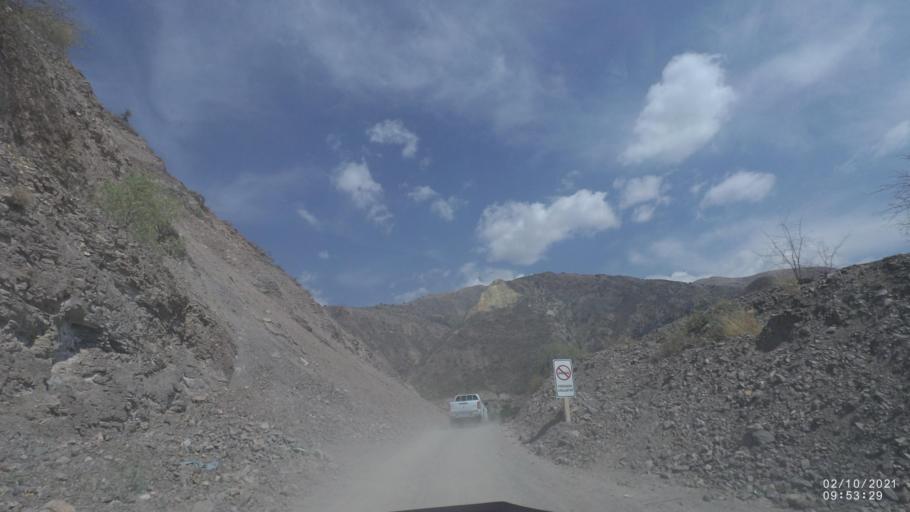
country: BO
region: Cochabamba
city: Irpa Irpa
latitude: -17.8013
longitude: -66.3493
